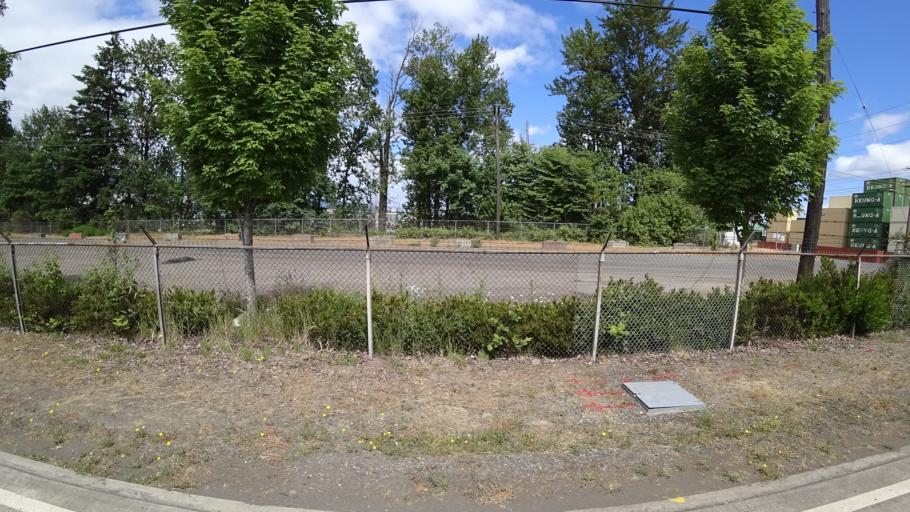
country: US
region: Oregon
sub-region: Washington County
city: West Haven
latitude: 45.6068
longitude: -122.7672
